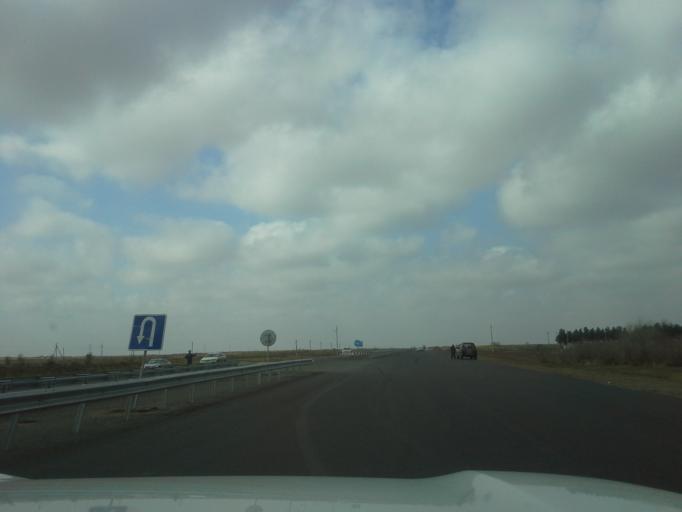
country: TM
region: Mary
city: Mary
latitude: 37.4286
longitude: 61.6025
